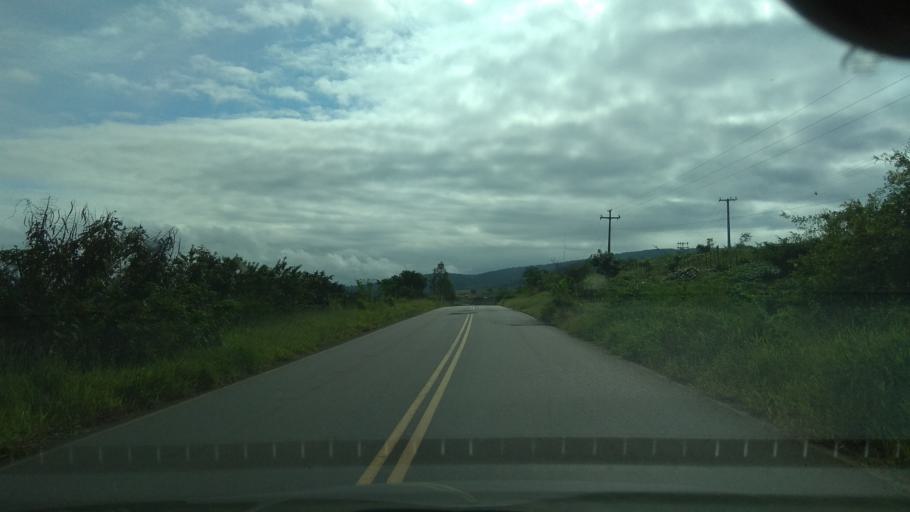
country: BR
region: Bahia
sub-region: Santa Ines
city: Santa Ines
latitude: -13.3511
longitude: -39.8759
